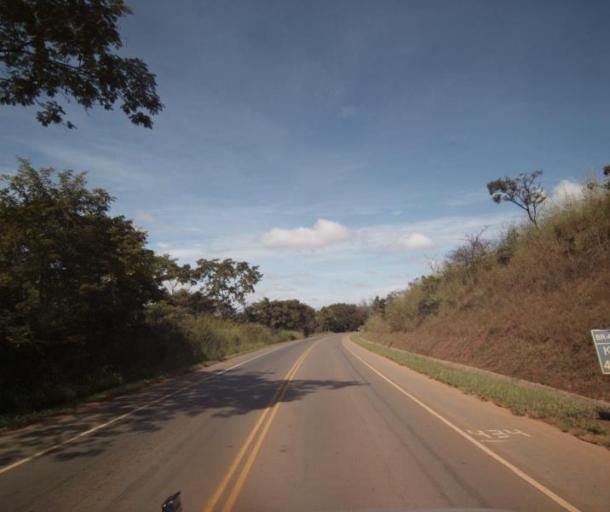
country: BR
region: Goias
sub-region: Anapolis
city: Anapolis
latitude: -16.2326
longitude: -48.9301
